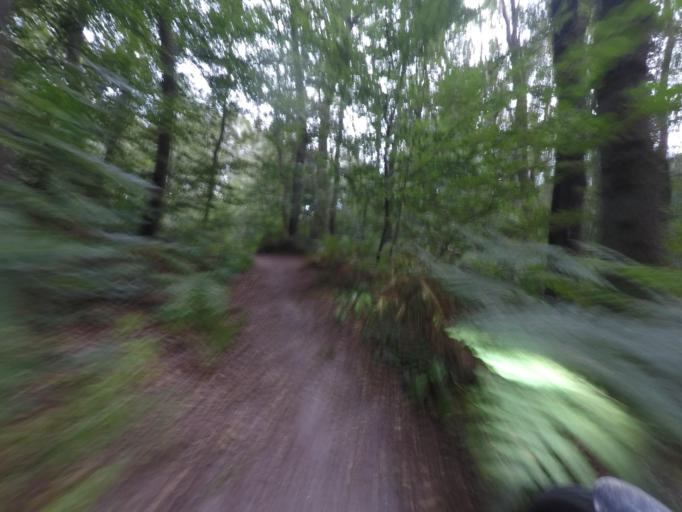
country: DE
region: Schleswig-Holstein
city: Stapelfeld
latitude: 53.6215
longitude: 10.1825
